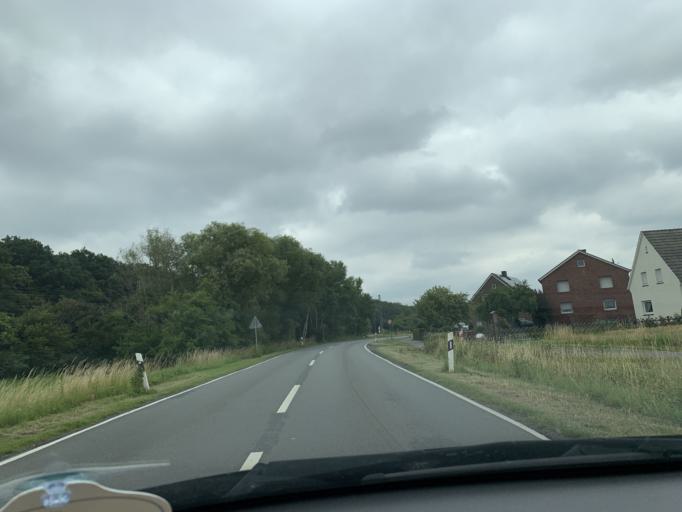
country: DE
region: North Rhine-Westphalia
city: Oelde
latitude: 51.8221
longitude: 8.1031
